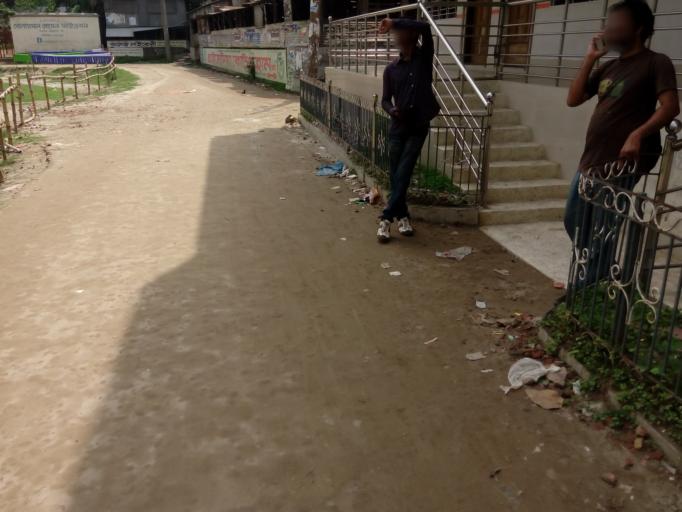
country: BD
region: Rajshahi
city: Sirajganj
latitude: 24.3285
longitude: 89.6860
